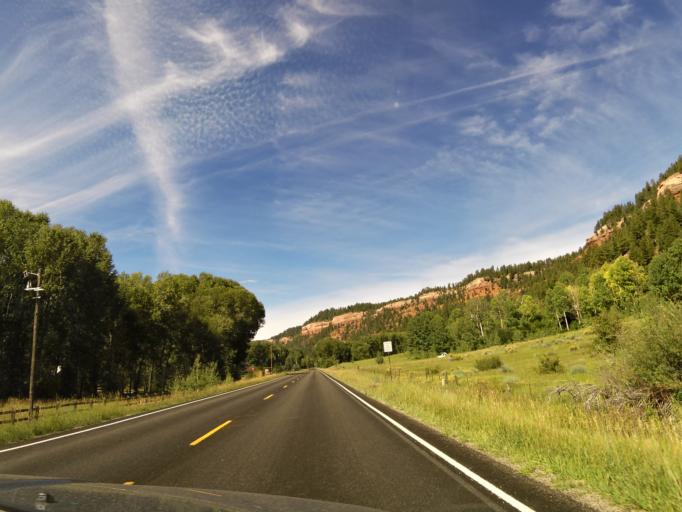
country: US
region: Colorado
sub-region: Montezuma County
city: Mancos
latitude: 37.5782
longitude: -108.2222
